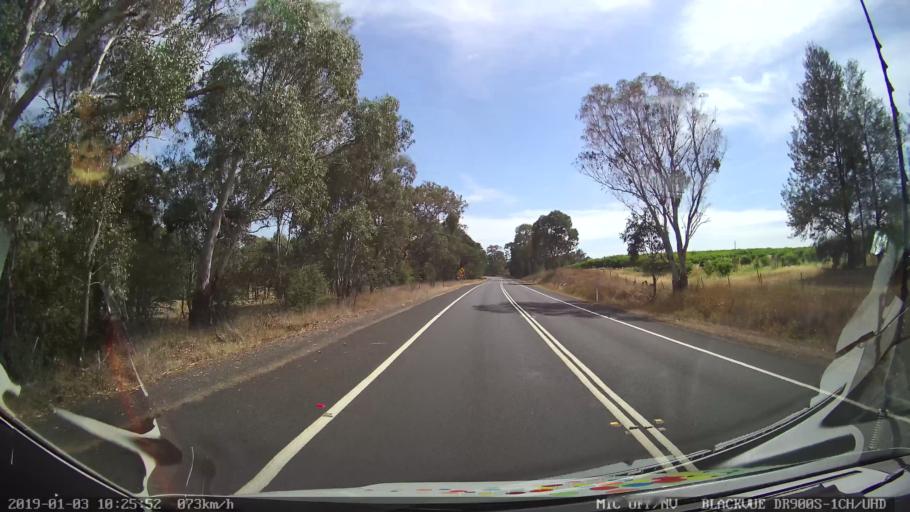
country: AU
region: New South Wales
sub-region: Young
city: Young
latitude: -34.4188
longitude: 148.2452
